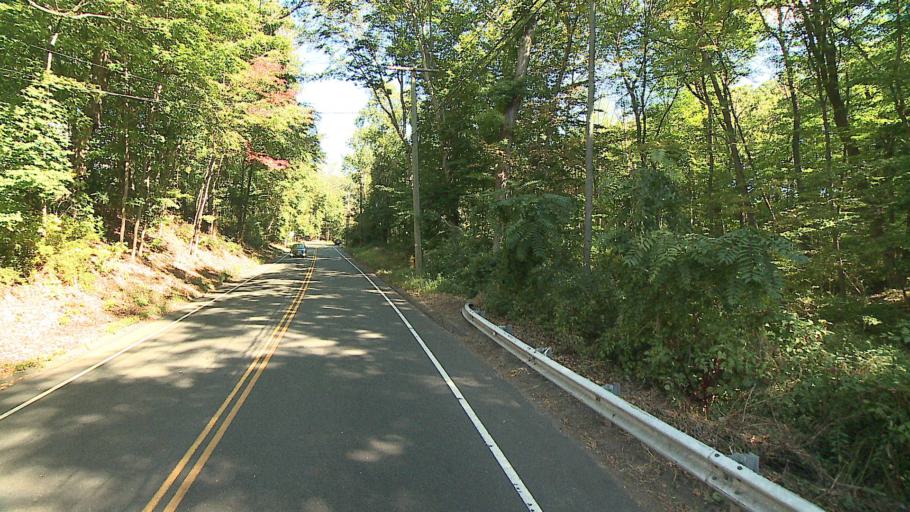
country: US
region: Connecticut
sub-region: Fairfield County
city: New Canaan
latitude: 41.1253
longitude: -73.4953
